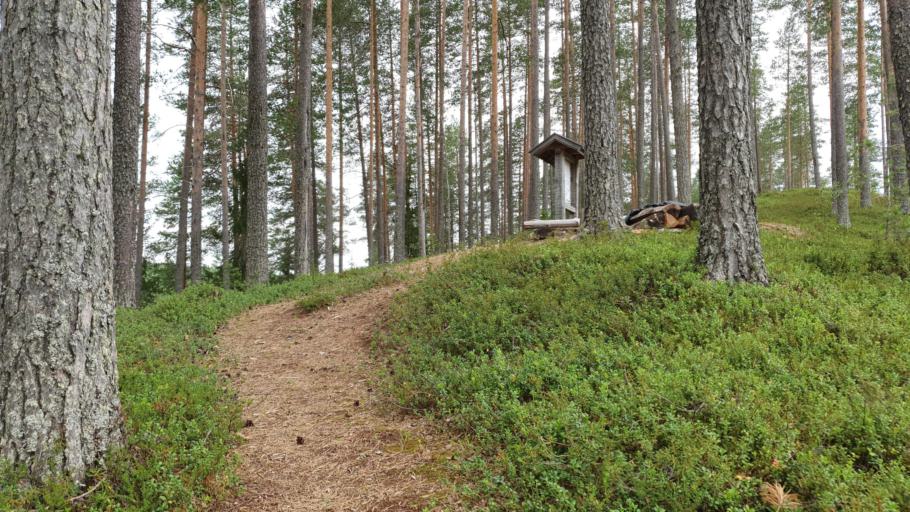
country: RU
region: Republic of Karelia
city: Kostomuksha
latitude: 64.7574
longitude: 30.0010
